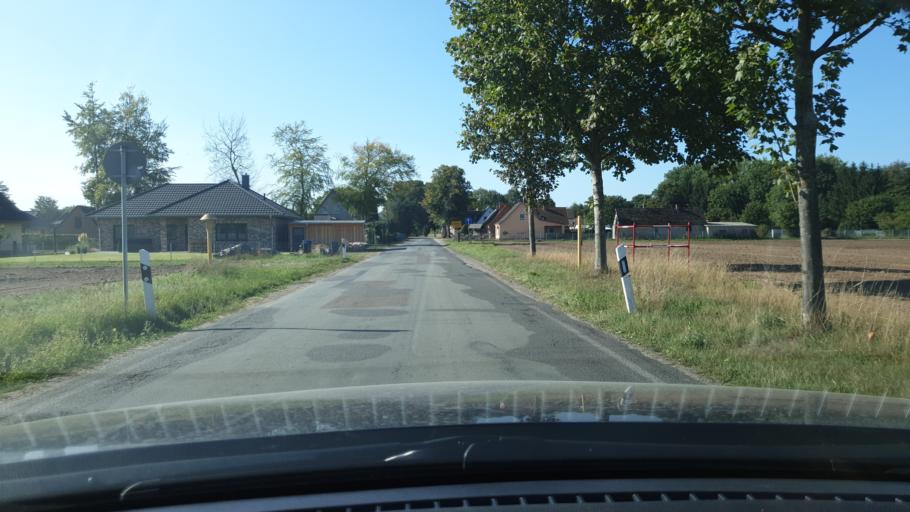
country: DE
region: Mecklenburg-Vorpommern
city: Wittenburg
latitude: 53.5048
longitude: 11.0035
